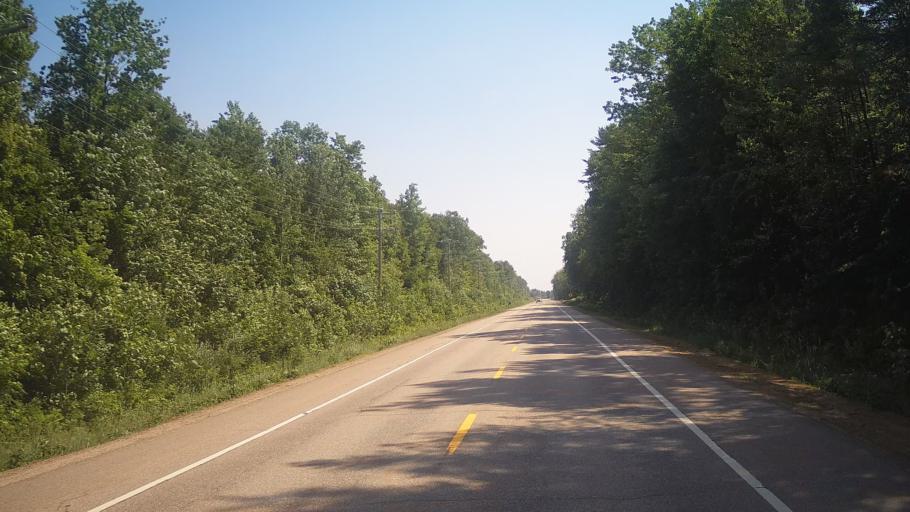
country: CA
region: Ontario
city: Pembroke
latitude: 45.8408
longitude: -77.0134
